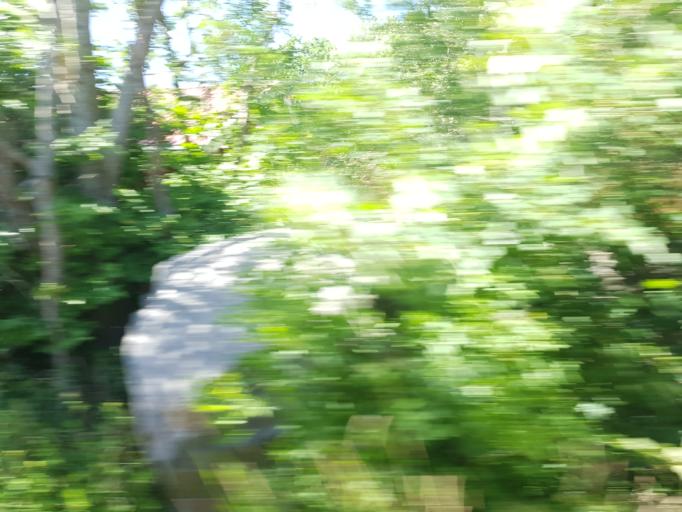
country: SE
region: Vaestra Goetaland
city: Ronnang
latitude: 57.9414
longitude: 11.5986
